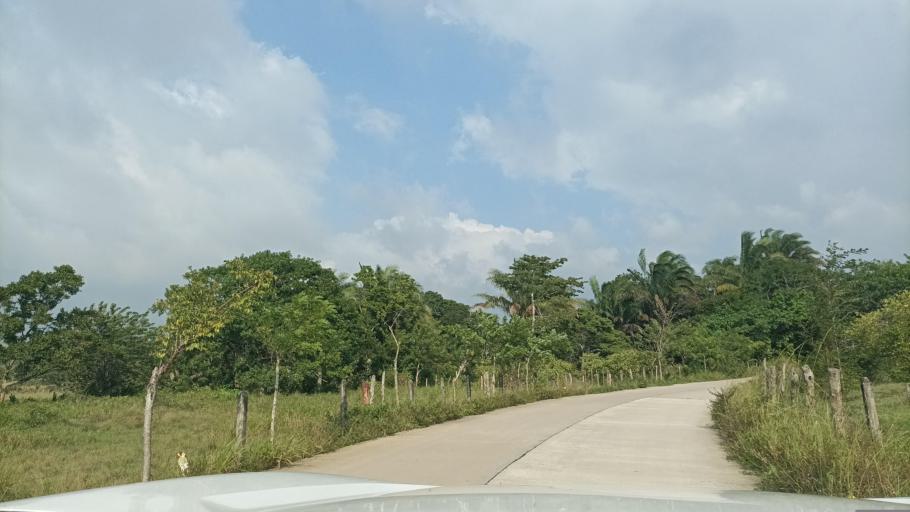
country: MX
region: Veracruz
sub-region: Moloacan
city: Tlacuilolapan
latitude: 18.0761
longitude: -94.2937
